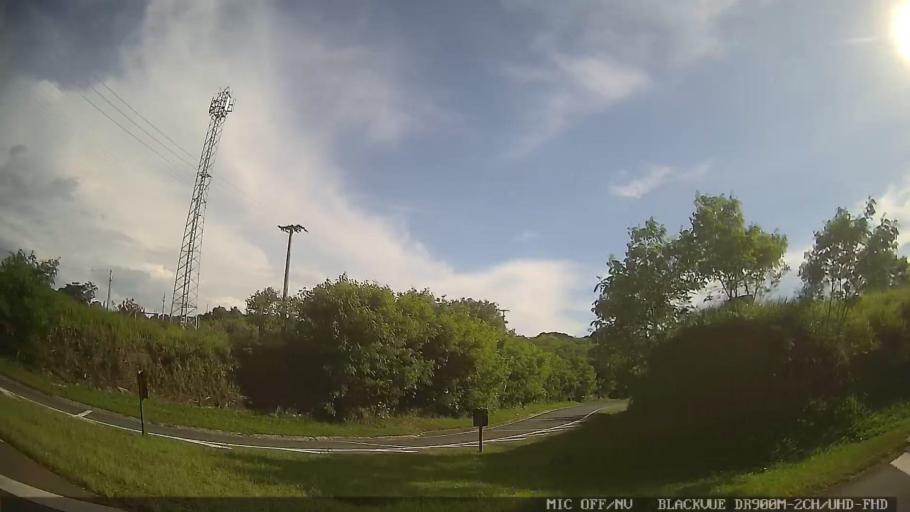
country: BR
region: Sao Paulo
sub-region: Tiete
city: Tiete
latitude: -23.1183
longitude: -47.7159
